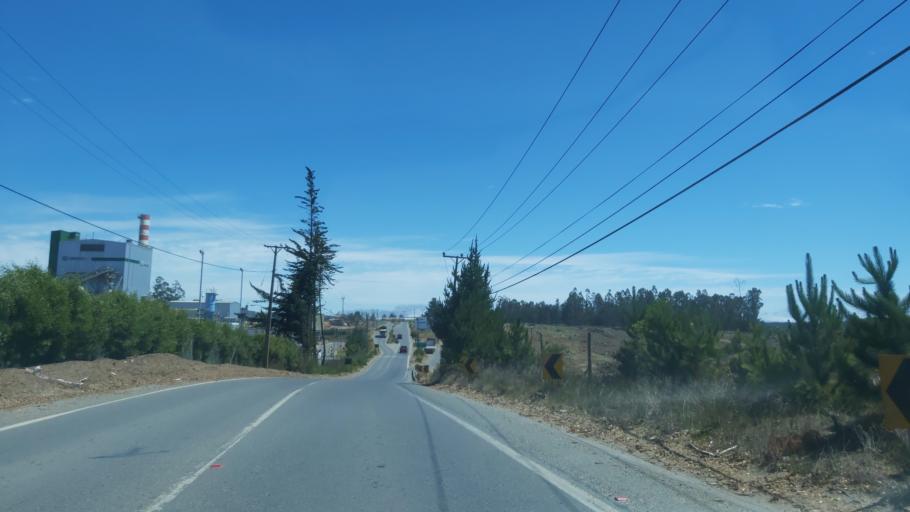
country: CL
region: Maule
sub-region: Provincia de Talca
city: Constitucion
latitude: -35.3681
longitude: -72.4096
